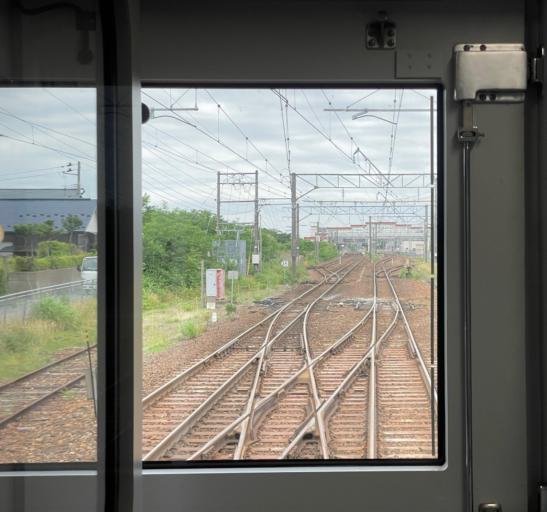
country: JP
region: Akita
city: Akita Shi
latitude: 39.8064
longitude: 140.0590
